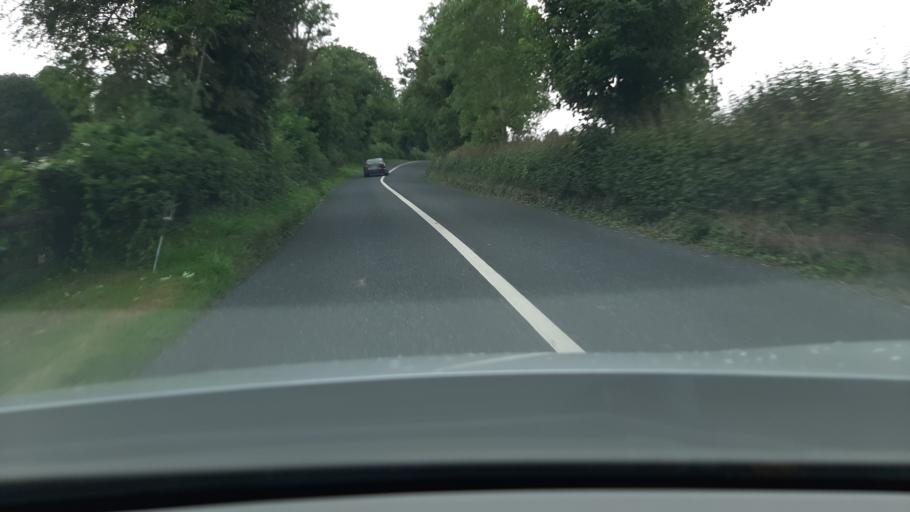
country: IE
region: Leinster
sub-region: Kildare
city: Rathangan
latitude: 53.2132
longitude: -6.9665
